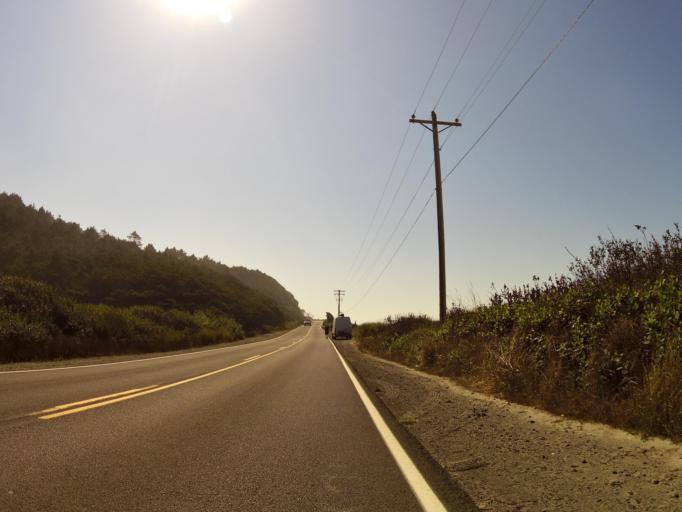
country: US
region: Oregon
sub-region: Tillamook County
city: Pacific City
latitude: 45.2427
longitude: -123.9685
